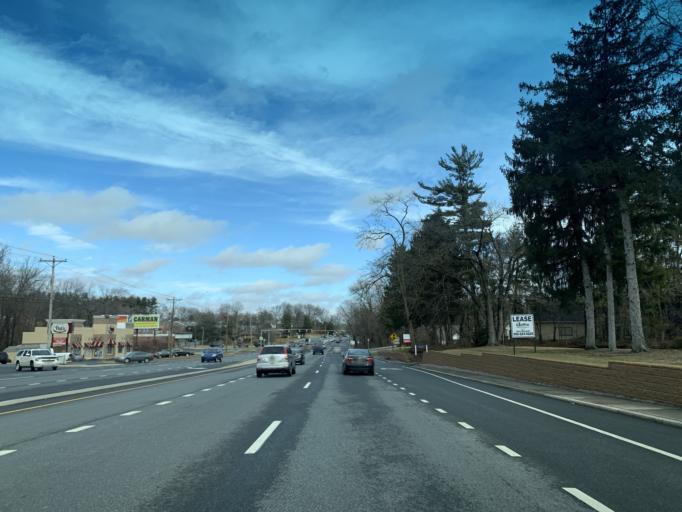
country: US
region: Delaware
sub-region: New Castle County
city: Pike Creek Valley
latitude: 39.7142
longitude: -75.6749
